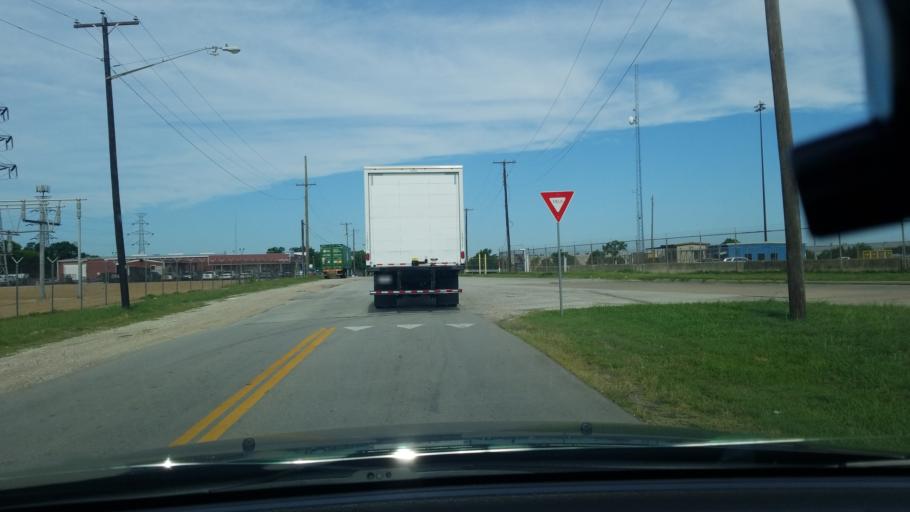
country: US
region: Texas
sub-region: Dallas County
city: Balch Springs
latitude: 32.7780
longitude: -96.6623
